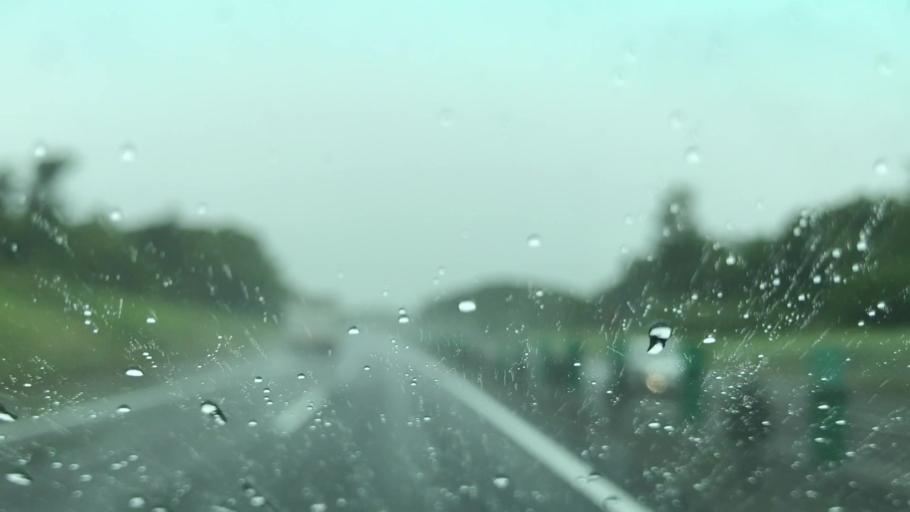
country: JP
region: Hokkaido
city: Chitose
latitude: 42.8319
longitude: 141.6109
